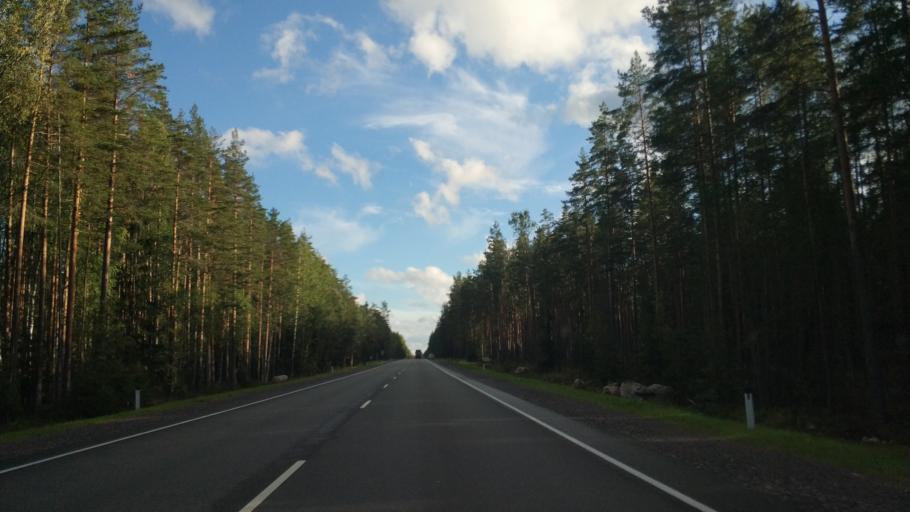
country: RU
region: Leningrad
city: Priozersk
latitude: 60.9044
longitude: 30.1602
